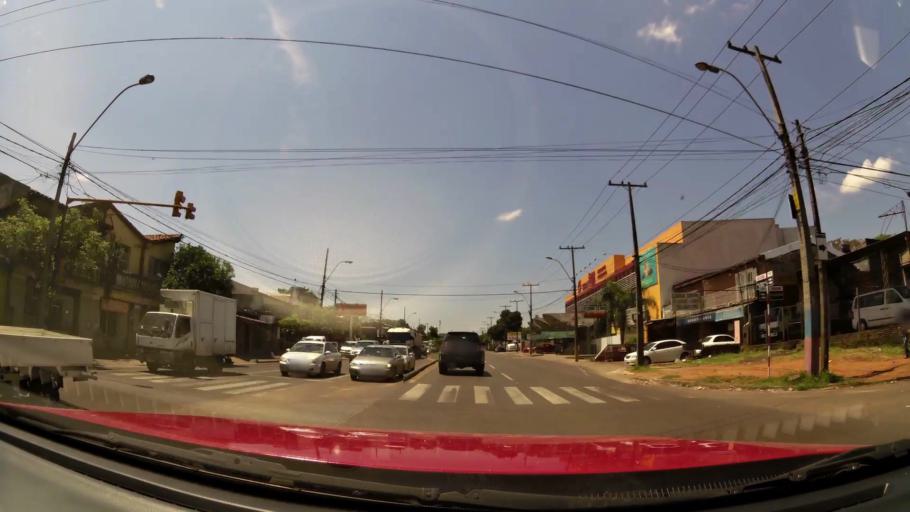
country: PY
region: Central
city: Lambare
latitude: -25.3340
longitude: -57.5782
